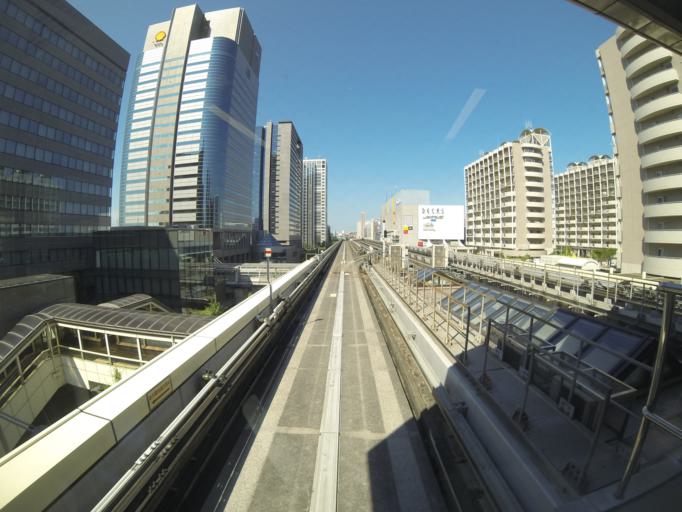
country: JP
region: Tokyo
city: Tokyo
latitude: 35.6281
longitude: 139.7756
